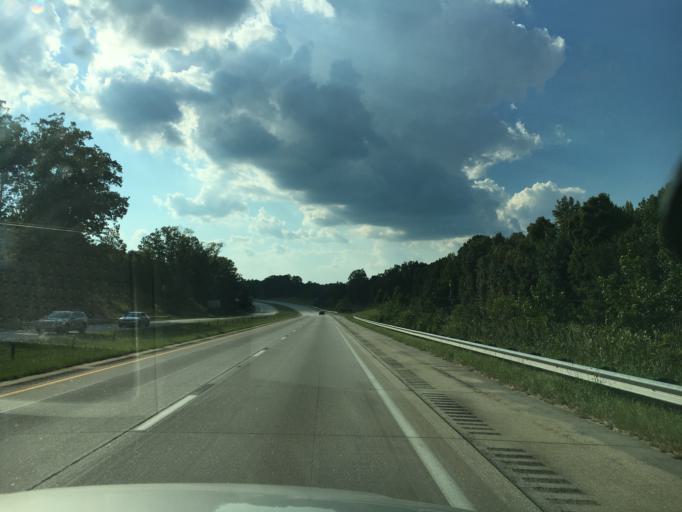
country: US
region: South Carolina
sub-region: Laurens County
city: Watts Mills
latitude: 34.5491
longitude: -81.9863
